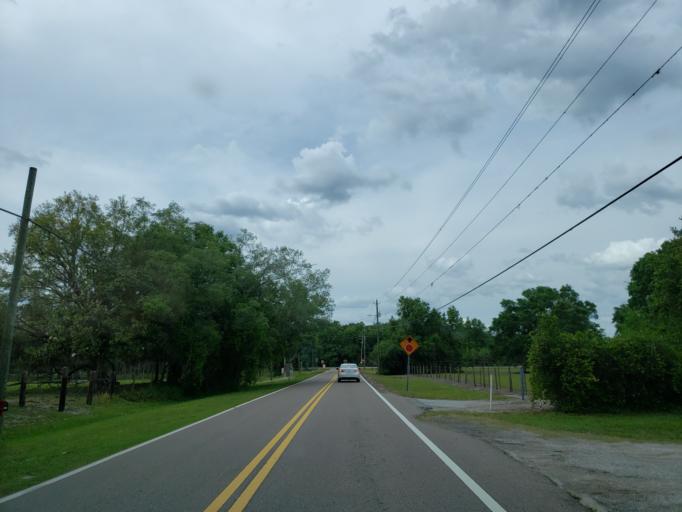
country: US
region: Florida
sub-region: Hillsborough County
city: Keystone
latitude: 28.1381
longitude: -82.6313
